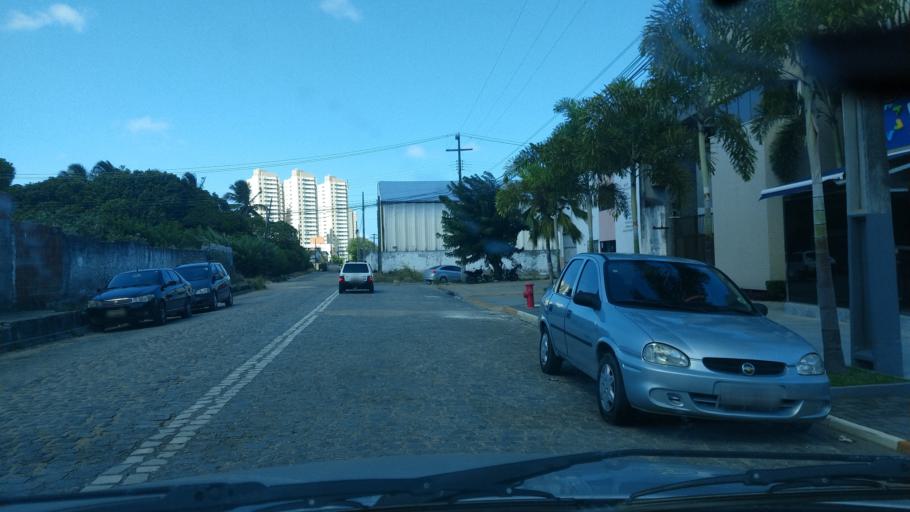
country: BR
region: Rio Grande do Norte
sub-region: Natal
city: Natal
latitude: -5.8581
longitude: -35.2144
